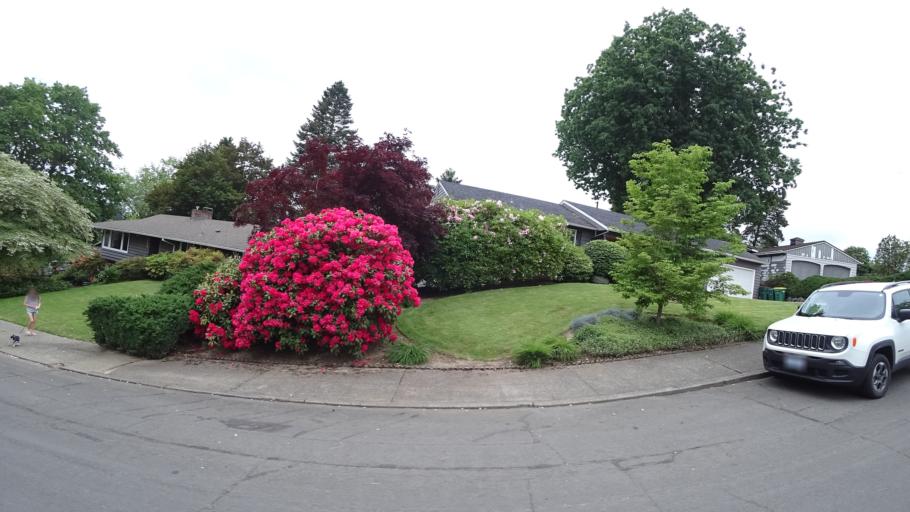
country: US
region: Oregon
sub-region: Washington County
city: Raleigh Hills
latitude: 45.4798
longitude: -122.7443
